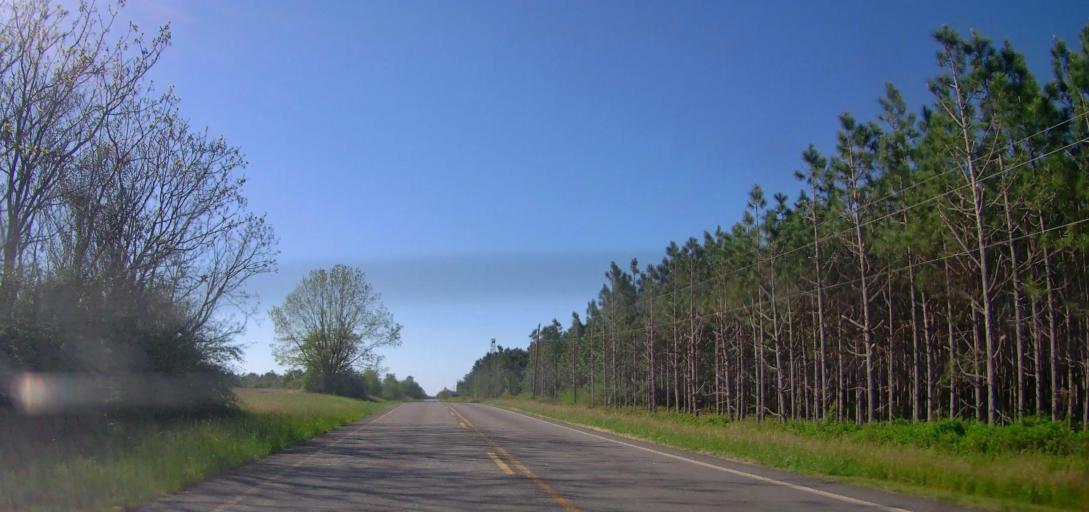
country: US
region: Georgia
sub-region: Wilcox County
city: Rochelle
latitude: 31.9993
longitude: -83.4781
